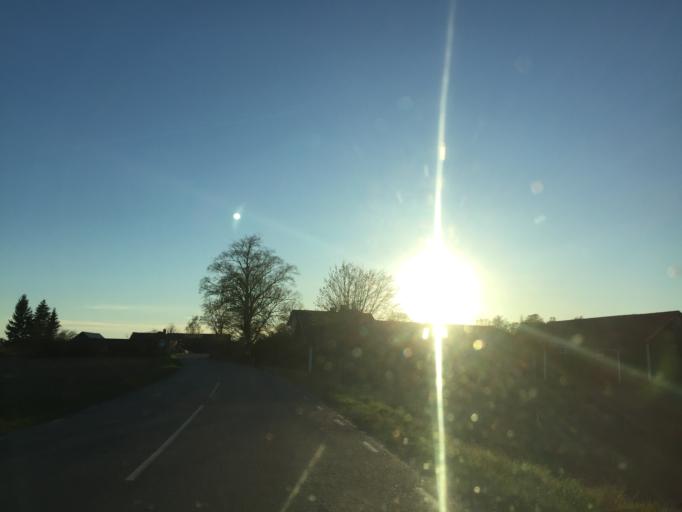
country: SE
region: OErebro
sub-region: Orebro Kommun
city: Odensbacken
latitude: 59.2049
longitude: 15.5238
